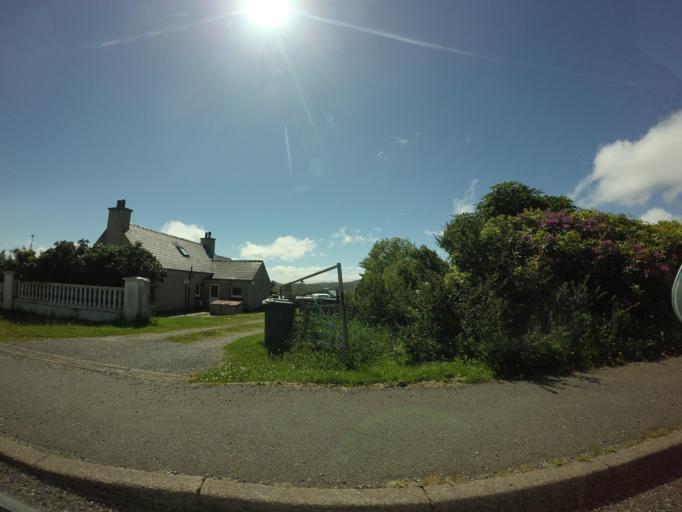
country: GB
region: Scotland
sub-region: Eilean Siar
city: Harris
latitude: 58.1888
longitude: -6.7053
